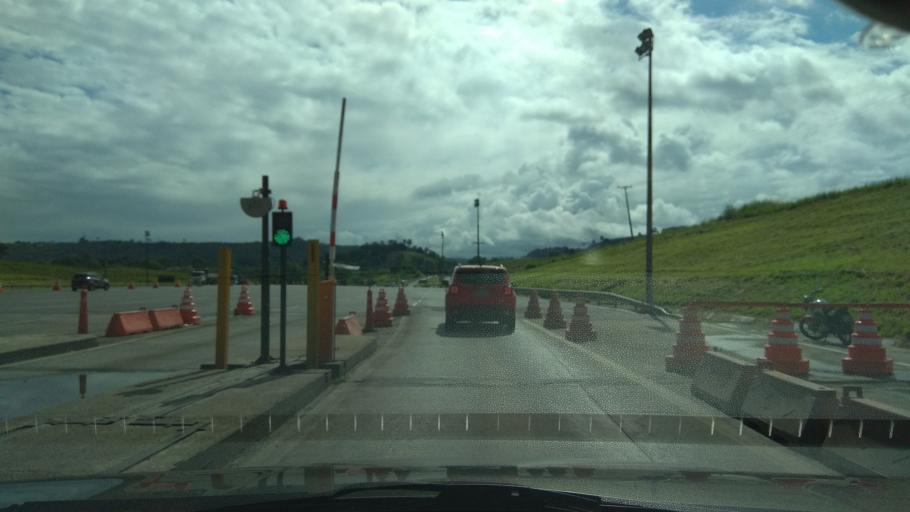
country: BR
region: Bahia
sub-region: Santo Amaro
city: Santo Amaro
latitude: -12.4510
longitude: -38.7086
